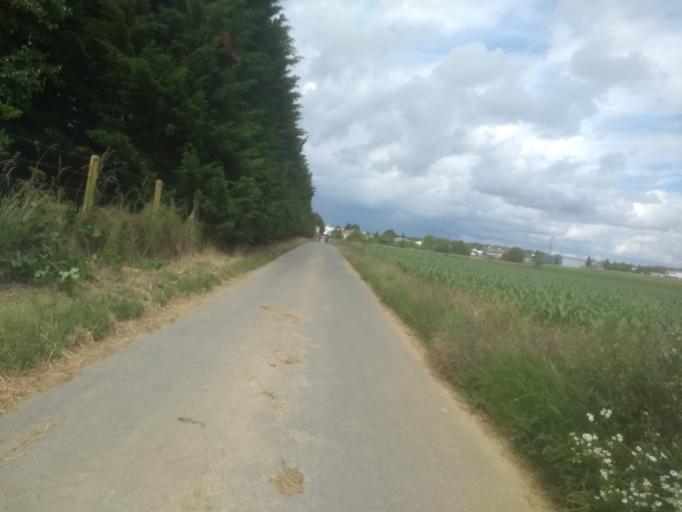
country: FR
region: Nord-Pas-de-Calais
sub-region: Departement du Pas-de-Calais
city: Dainville
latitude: 50.2668
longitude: 2.7161
